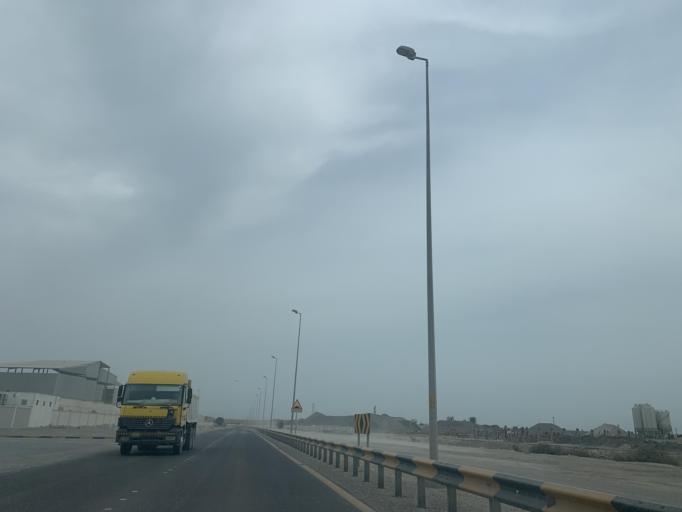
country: BH
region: Muharraq
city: Al Hadd
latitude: 26.2045
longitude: 50.6639
